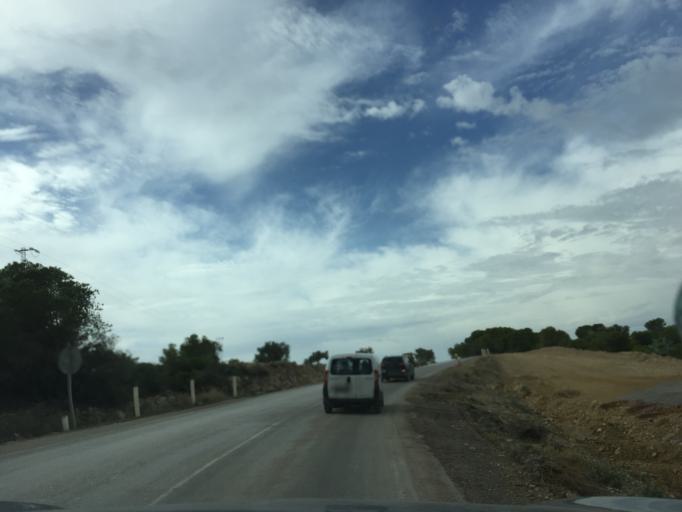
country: TN
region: Zaghwan
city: El Fahs
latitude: 36.2927
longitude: 9.8095
